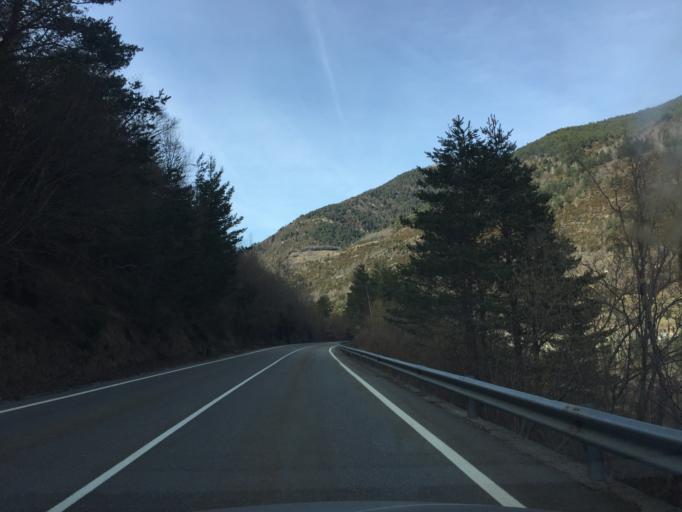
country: ES
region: Aragon
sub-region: Provincia de Huesca
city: Bielsa
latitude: 42.6247
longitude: 0.2282
